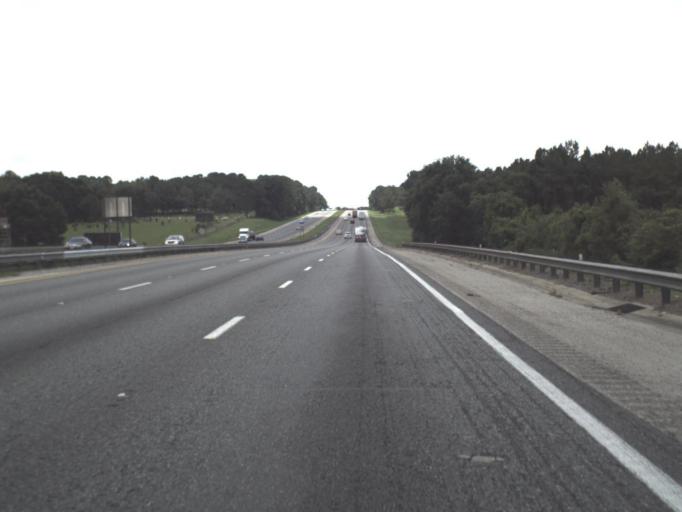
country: US
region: Florida
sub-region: Alachua County
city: Alachua
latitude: 29.7747
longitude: -82.5092
